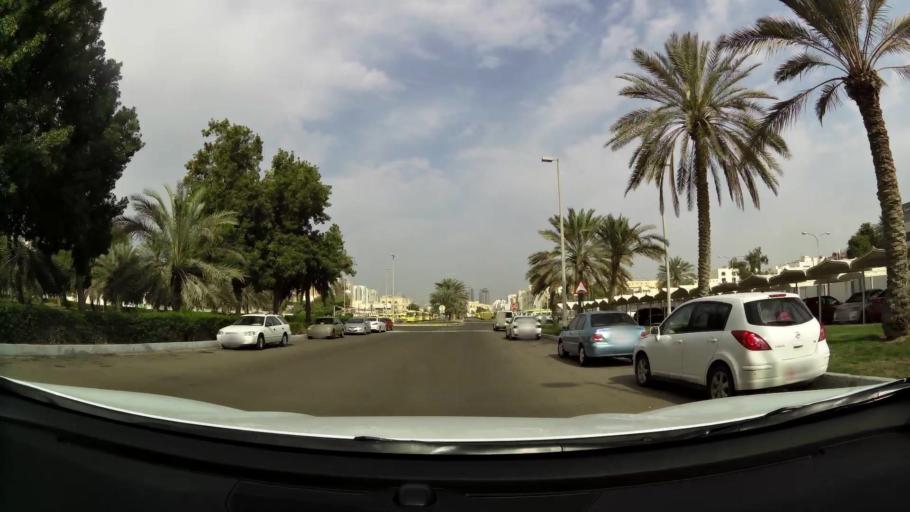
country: AE
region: Abu Dhabi
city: Abu Dhabi
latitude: 24.4562
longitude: 54.3875
